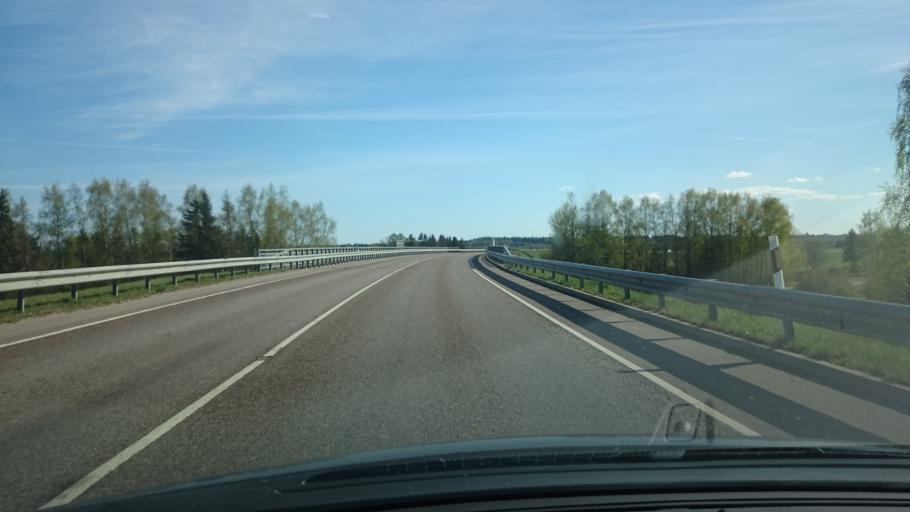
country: EE
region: Laeaene-Virumaa
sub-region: Kadrina vald
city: Kadrina
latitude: 59.3377
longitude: 26.1195
